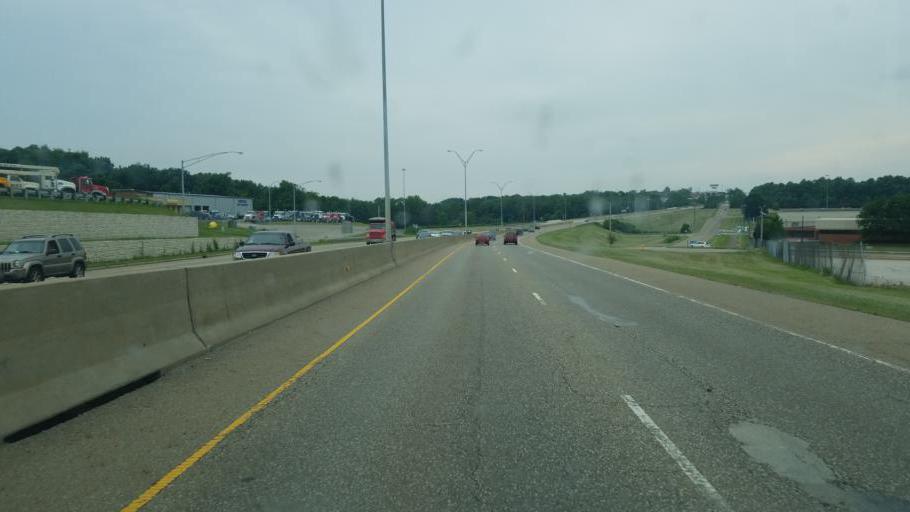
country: US
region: Ohio
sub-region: Summit County
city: Sawyerwood
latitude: 41.0256
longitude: -81.4687
